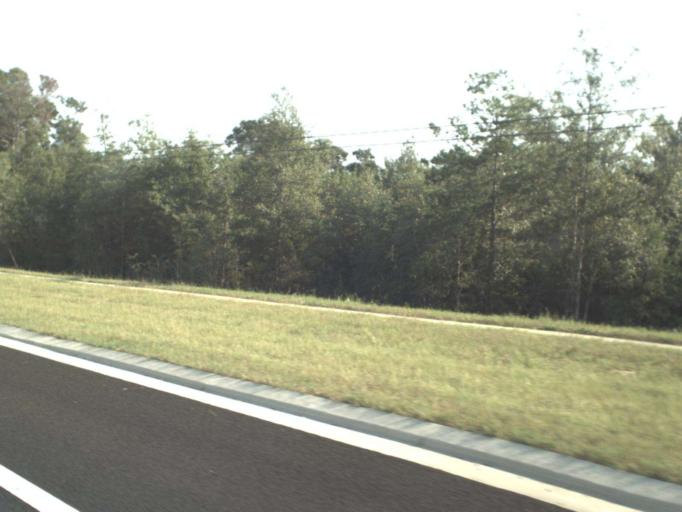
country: US
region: Florida
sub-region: Holmes County
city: Bonifay
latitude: 30.5689
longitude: -85.8067
